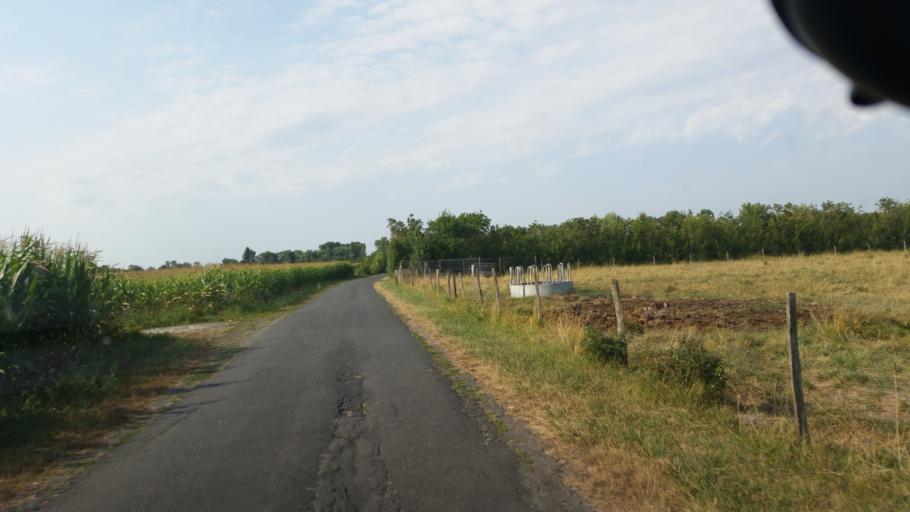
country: FR
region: Poitou-Charentes
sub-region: Departement de la Charente-Maritime
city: Saint-Jean-de-Liversay
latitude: 46.3113
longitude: -0.8962
